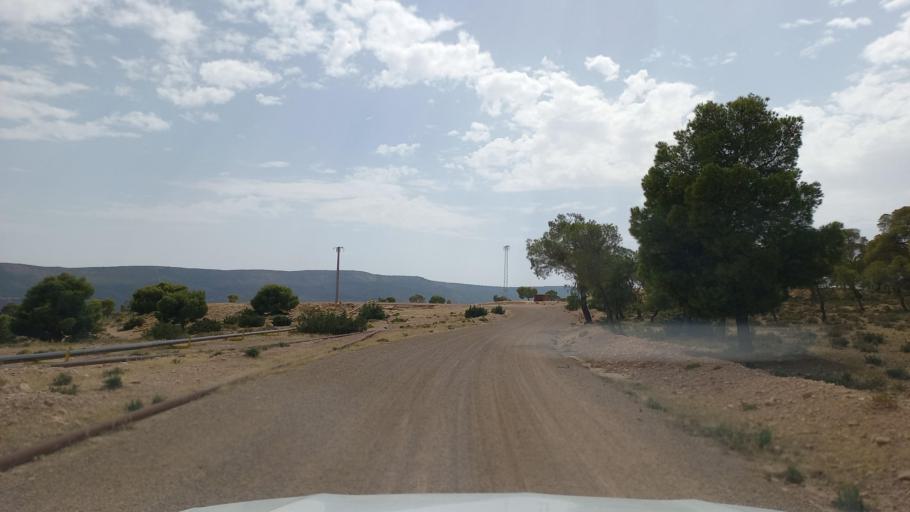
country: TN
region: Al Qasrayn
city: Kasserine
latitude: 35.3785
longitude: 8.8797
